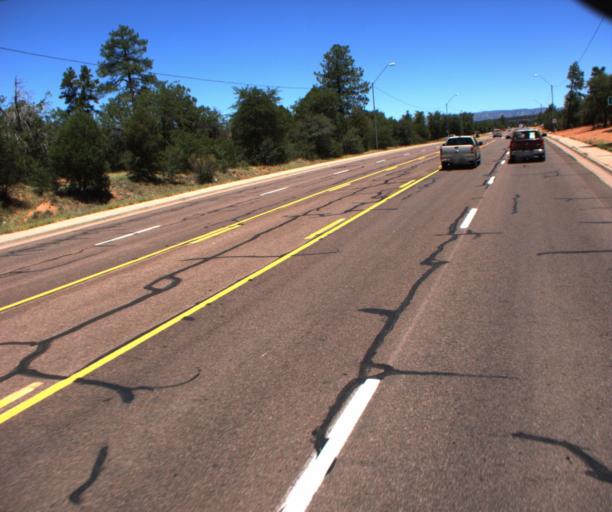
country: US
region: Arizona
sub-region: Gila County
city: Payson
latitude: 34.2605
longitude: -111.3222
